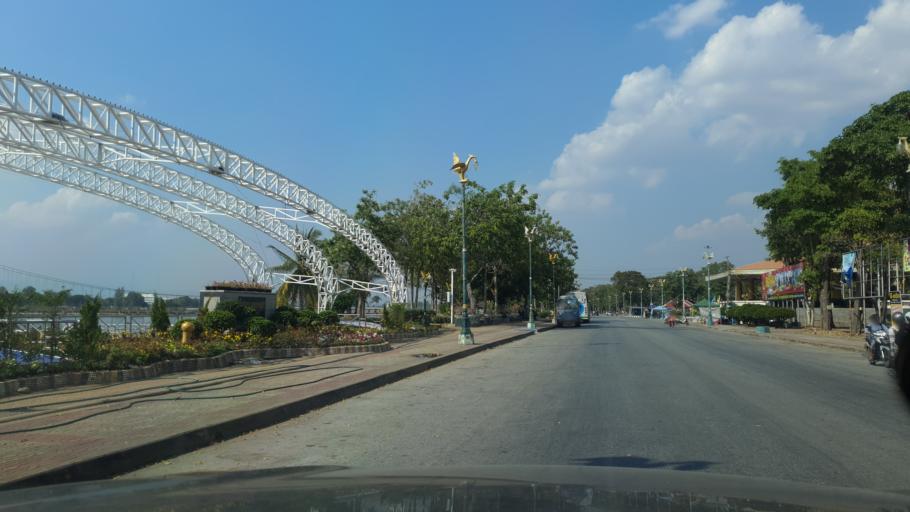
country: TH
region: Tak
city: Tak
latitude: 16.8771
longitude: 99.1212
